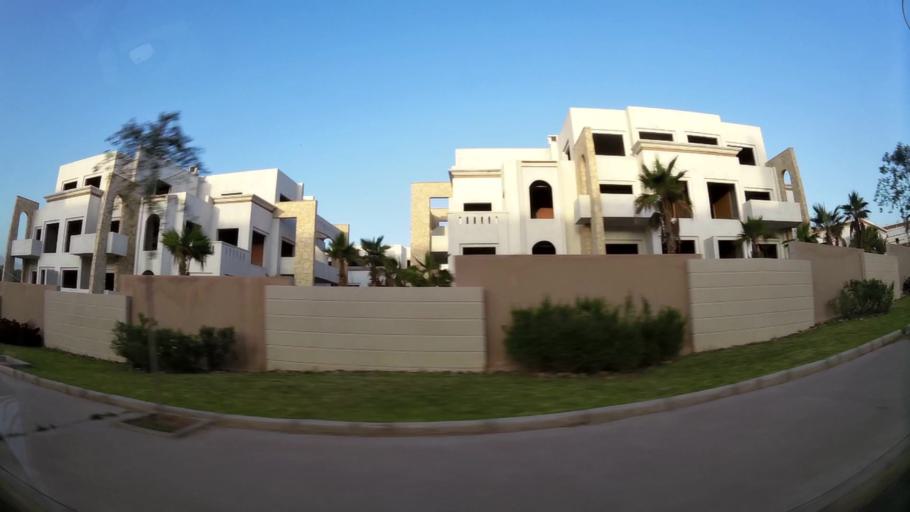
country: MA
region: Souss-Massa-Draa
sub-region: Agadir-Ida-ou-Tnan
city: Agadir
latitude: 30.4031
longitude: -9.5930
